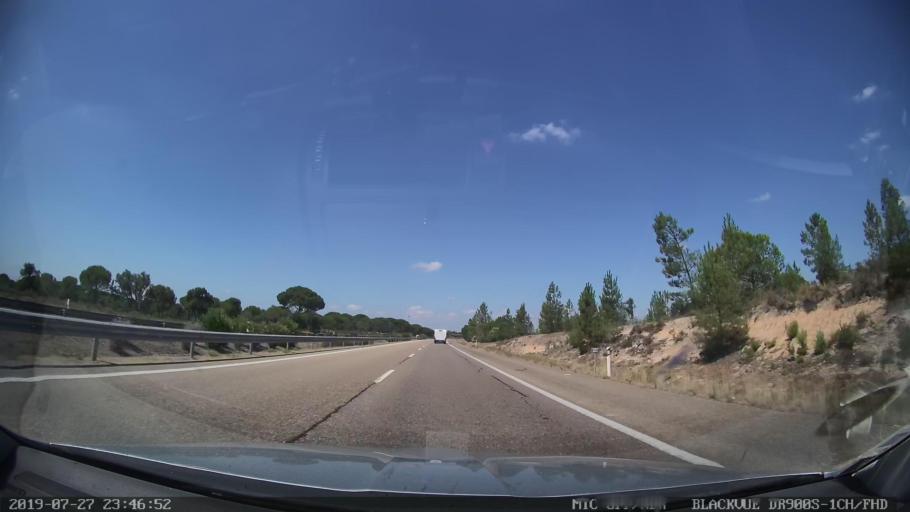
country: PT
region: Evora
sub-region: Vendas Novas
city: Vendas Novas
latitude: 38.6346
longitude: -8.5131
